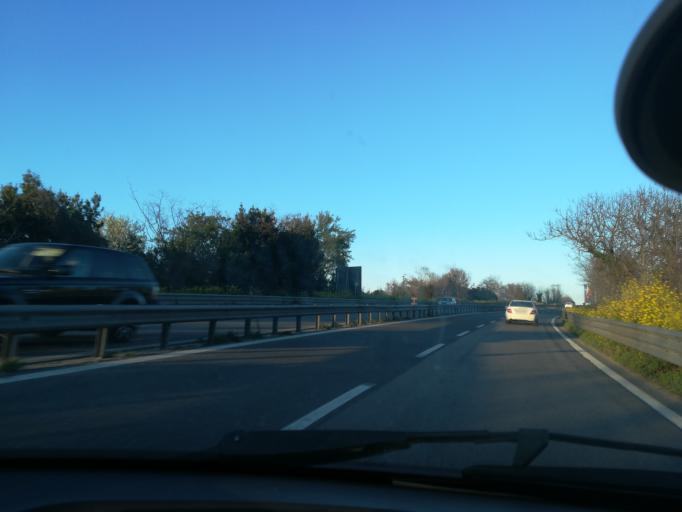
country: IT
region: The Marches
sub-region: Provincia di Macerata
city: Civitanova Marche
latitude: 43.2929
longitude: 13.7167
